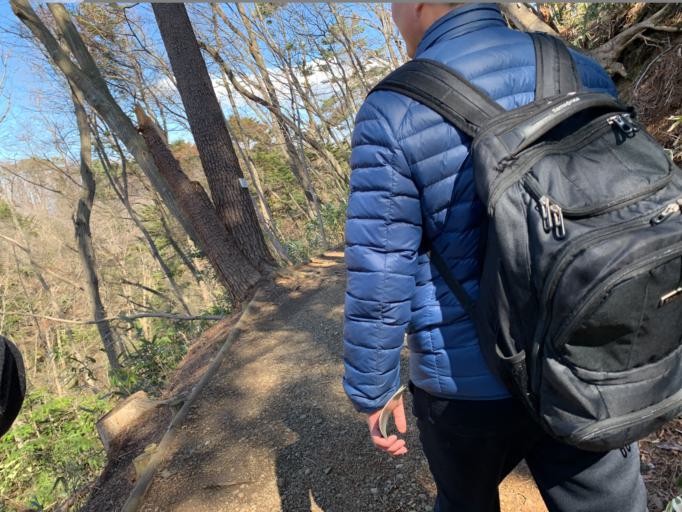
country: JP
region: Miyagi
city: Sendai
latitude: 38.2542
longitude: 140.8467
